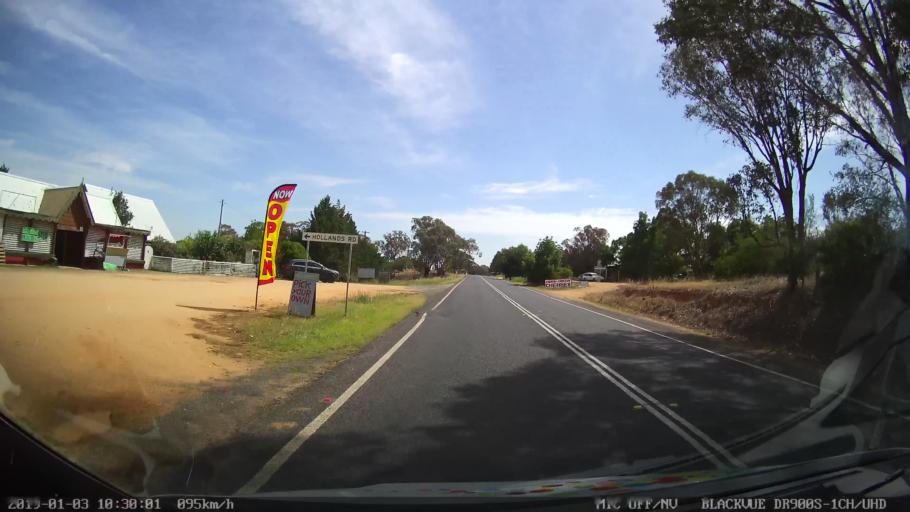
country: AU
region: New South Wales
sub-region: Young
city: Young
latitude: -34.3668
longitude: 148.2636
